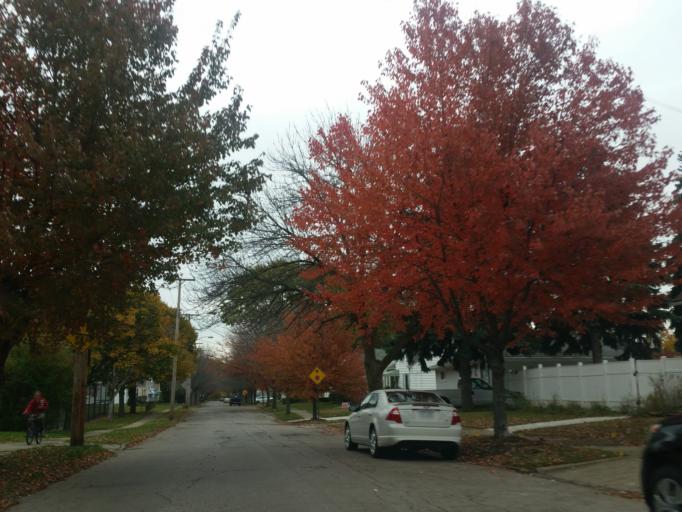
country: US
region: Ohio
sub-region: Cuyahoga County
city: Brooklyn Heights
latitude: 41.4376
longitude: -81.6937
